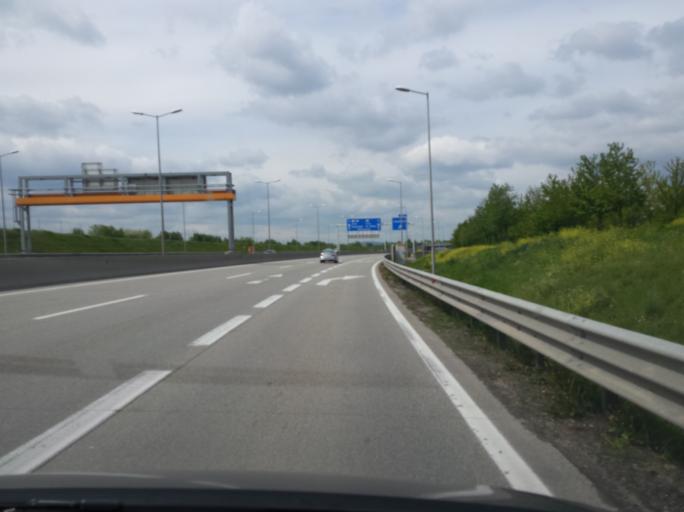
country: AT
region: Lower Austria
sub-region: Politischer Bezirk Wien-Umgebung
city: Leopoldsdorf
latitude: 48.1205
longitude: 16.4108
